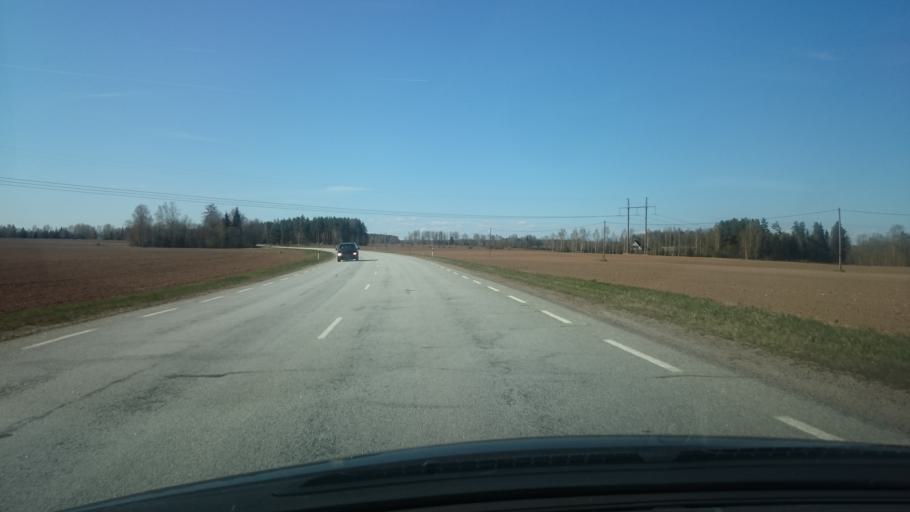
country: EE
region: Polvamaa
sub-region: Polva linn
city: Polva
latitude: 58.3075
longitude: 26.9995
